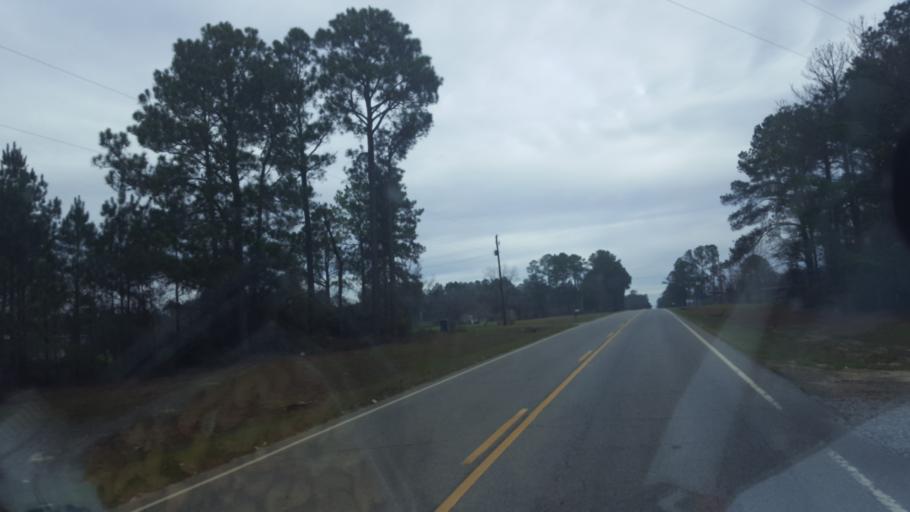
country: US
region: Georgia
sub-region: Wilcox County
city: Rochelle
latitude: 31.7985
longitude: -83.4952
